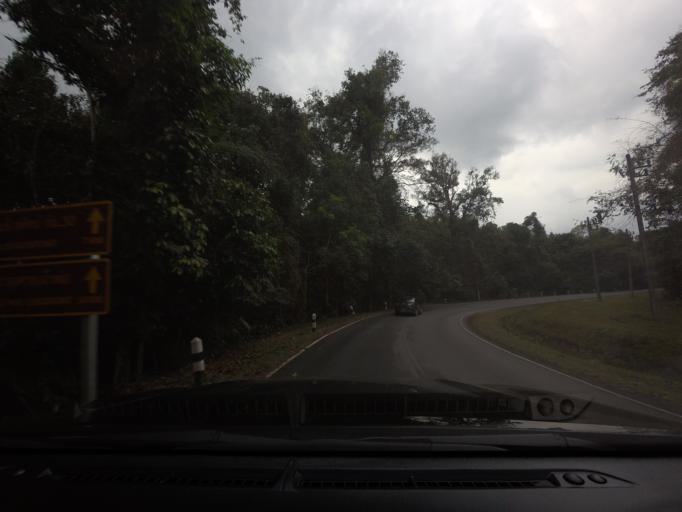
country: TH
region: Nakhon Ratchasima
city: Pak Chong
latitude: 14.4380
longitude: 101.3703
